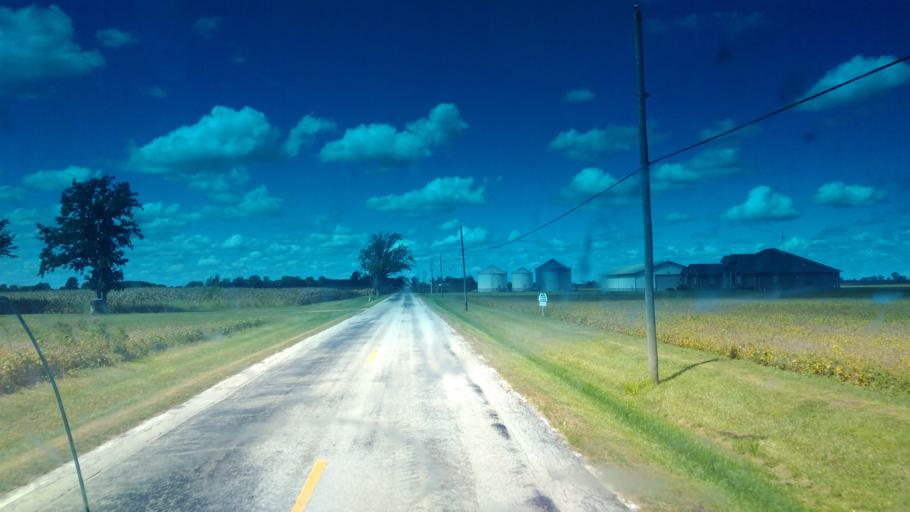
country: US
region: Ohio
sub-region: Madison County
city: West Jefferson
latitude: 39.9976
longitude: -83.3478
